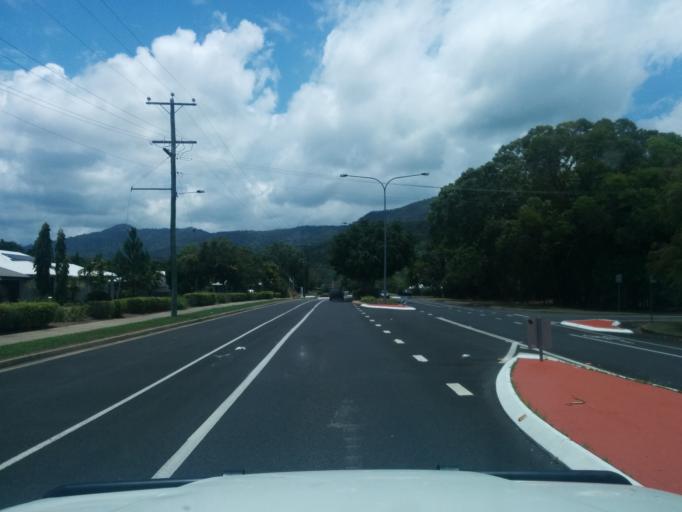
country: AU
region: Queensland
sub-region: Cairns
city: Trinity Beach
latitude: -16.8080
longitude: 145.6981
